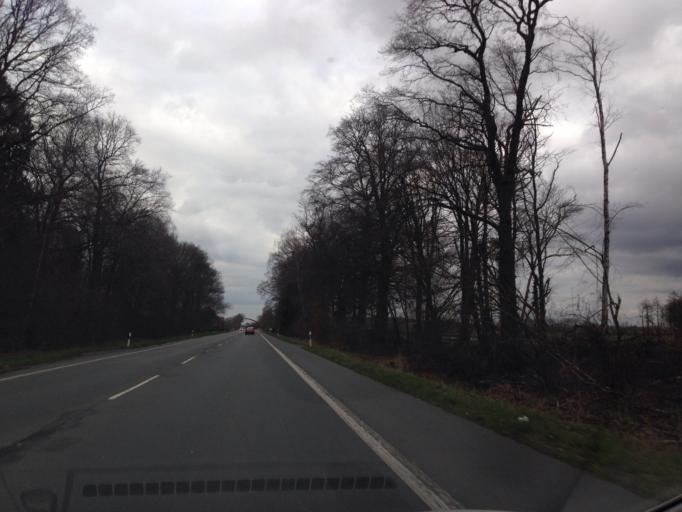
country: DE
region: North Rhine-Westphalia
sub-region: Regierungsbezirk Munster
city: Senden
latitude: 51.8706
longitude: 7.5547
